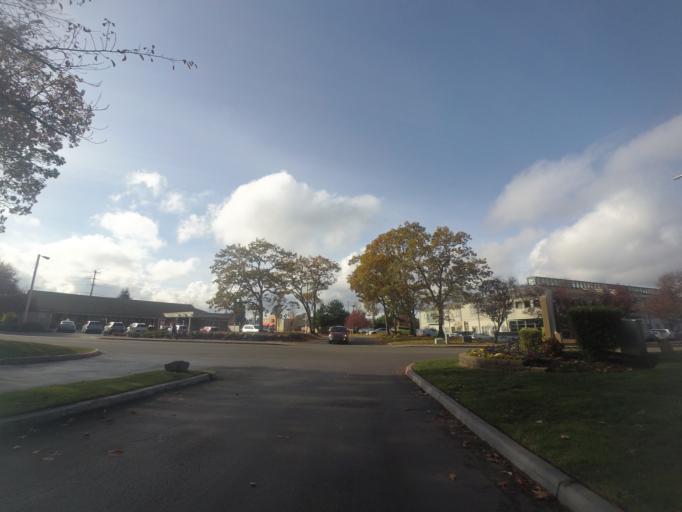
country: US
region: Washington
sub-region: Pierce County
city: Lakewood
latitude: 47.1713
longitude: -122.5153
